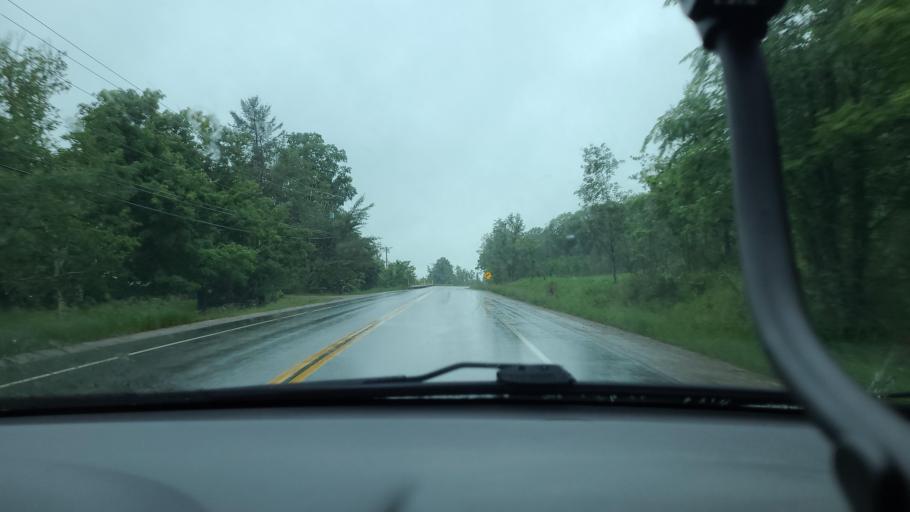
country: CA
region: Quebec
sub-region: Outaouais
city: Saint-Andre-Avellin
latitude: 45.8418
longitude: -75.0519
